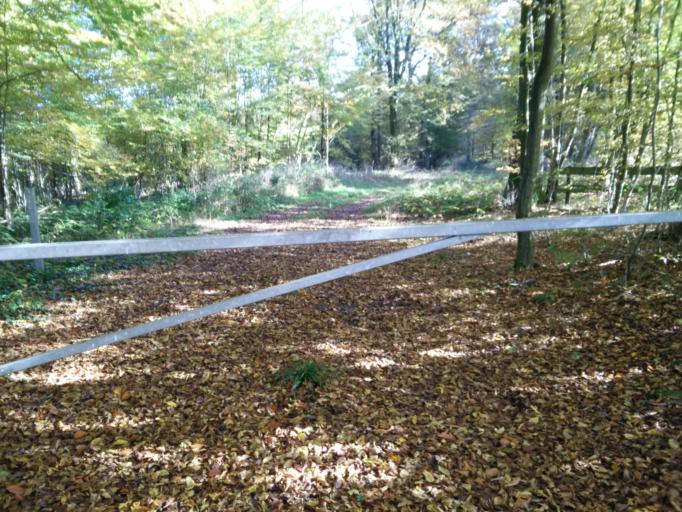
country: FR
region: Nord-Pas-de-Calais
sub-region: Departement du Nord
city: Trelon
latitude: 50.1329
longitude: 4.1462
